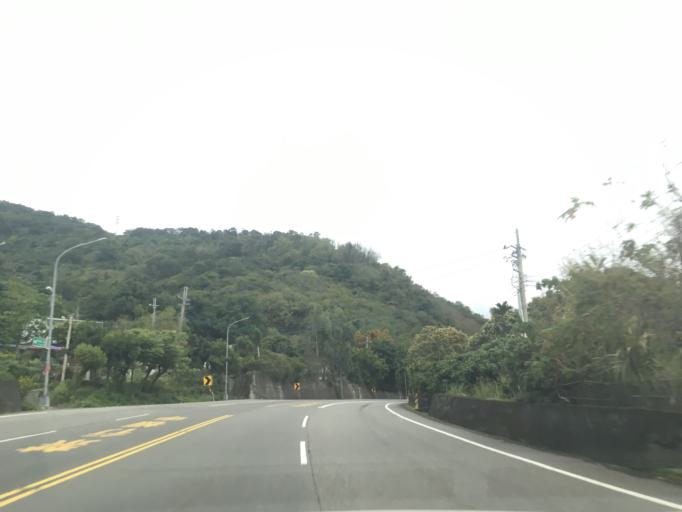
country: TW
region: Taiwan
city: Taitung City
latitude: 22.7489
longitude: 121.0551
